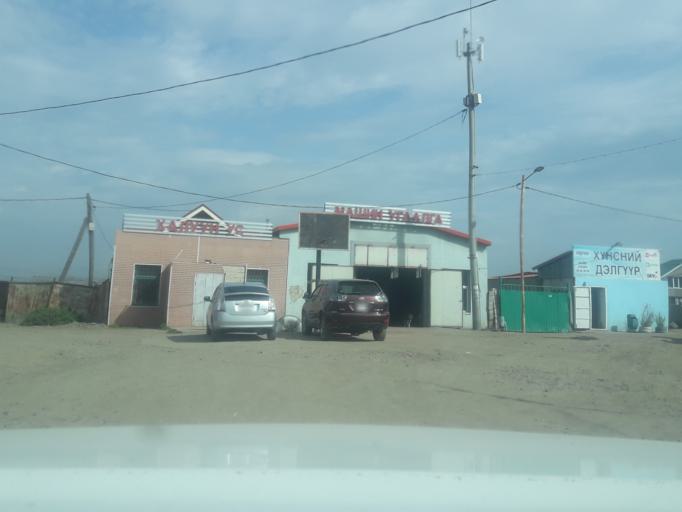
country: MN
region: Ulaanbaatar
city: Ulaanbaatar
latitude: 47.8733
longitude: 106.8067
